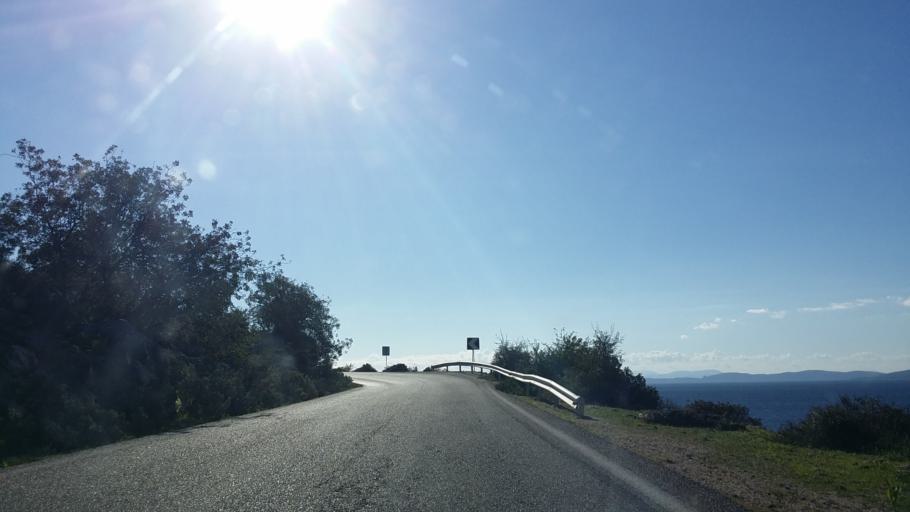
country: GR
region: West Greece
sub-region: Nomos Aitolias kai Akarnanias
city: Kandila
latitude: 38.7159
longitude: 20.8945
